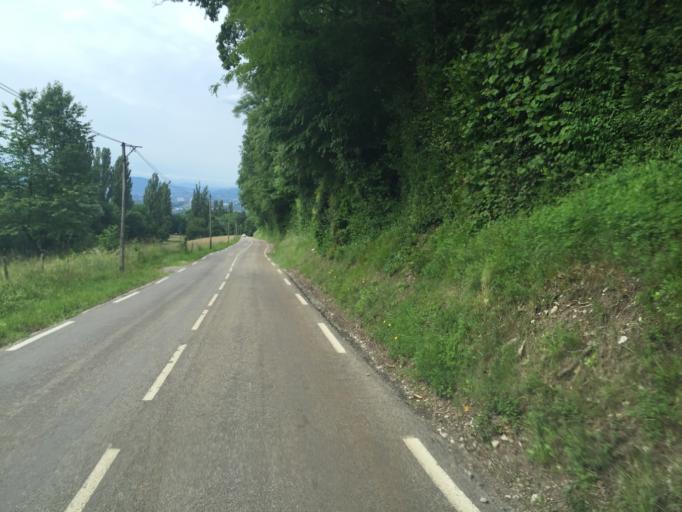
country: FR
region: Rhone-Alpes
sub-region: Departement de la Savoie
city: Jacob-Bellecombette
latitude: 45.5355
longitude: 5.9159
